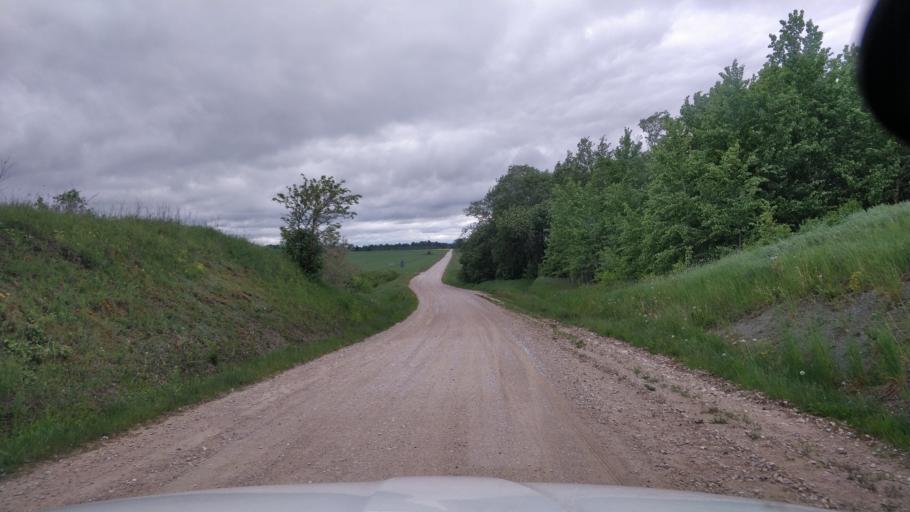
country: EE
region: Raplamaa
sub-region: Maerjamaa vald
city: Marjamaa
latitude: 58.7157
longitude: 24.2315
